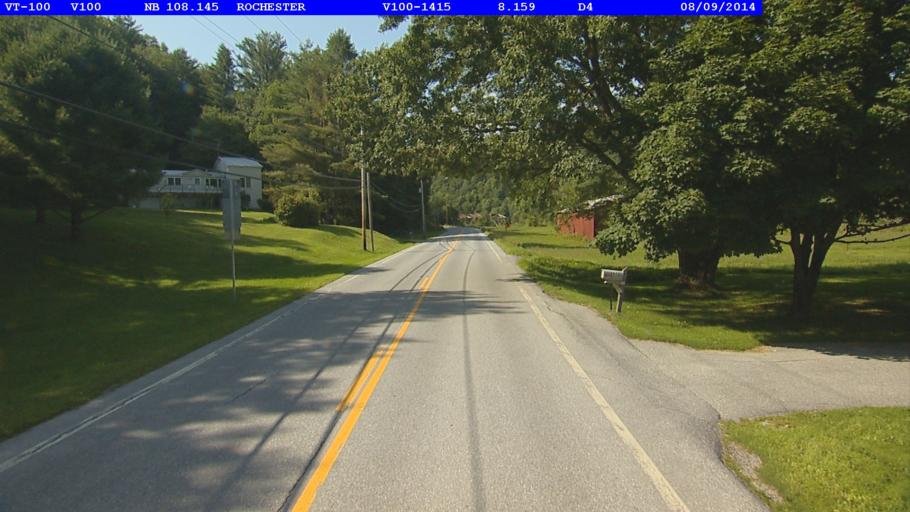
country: US
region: Vermont
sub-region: Orange County
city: Randolph
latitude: 43.9100
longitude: -72.8308
